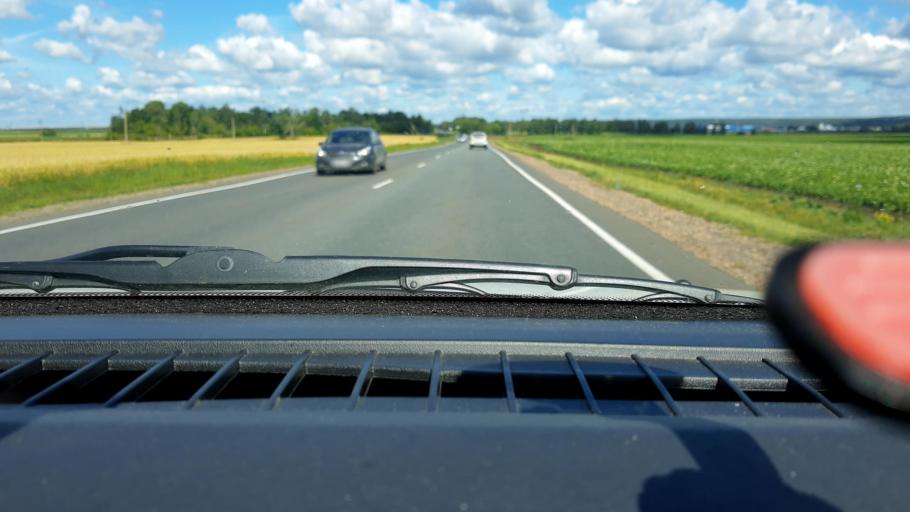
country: RU
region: Nizjnij Novgorod
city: Arzamas
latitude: 55.2794
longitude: 43.9566
